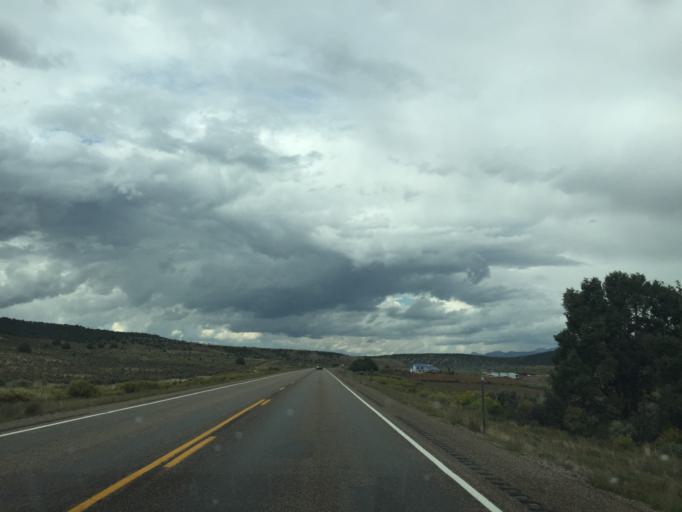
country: US
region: Utah
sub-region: Garfield County
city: Panguitch
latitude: 37.7357
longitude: -112.3797
